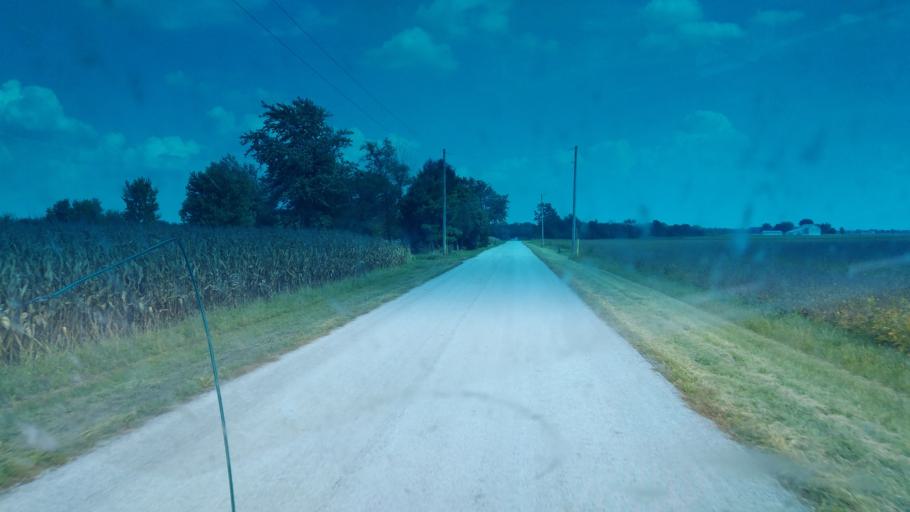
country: US
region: Ohio
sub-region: Hardin County
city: Kenton
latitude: 40.6607
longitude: -83.6845
